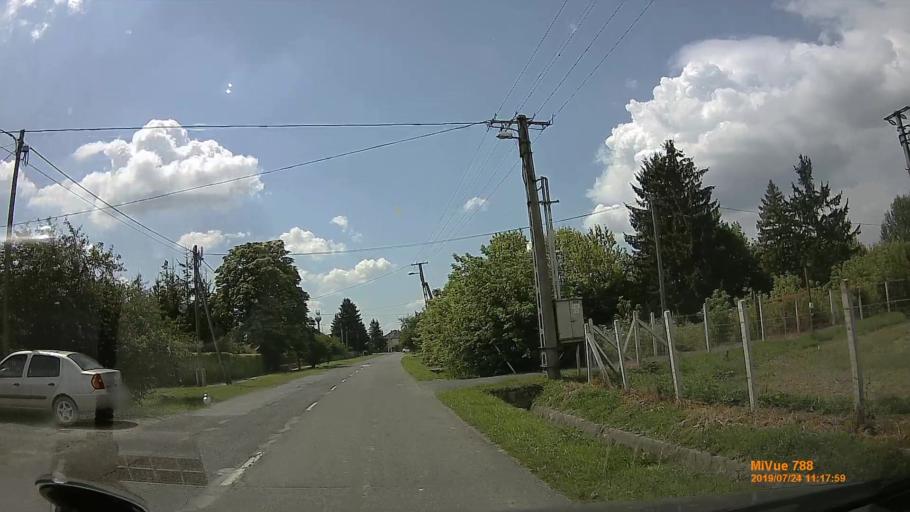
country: HU
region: Szabolcs-Szatmar-Bereg
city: Tarpa
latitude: 48.1657
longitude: 22.4588
